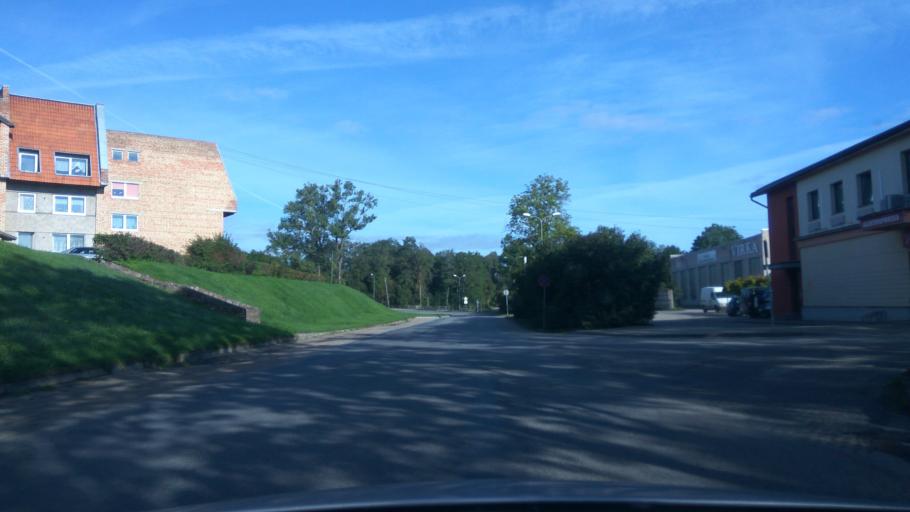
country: LV
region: Kuldigas Rajons
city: Kuldiga
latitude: 56.9771
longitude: 21.9620
